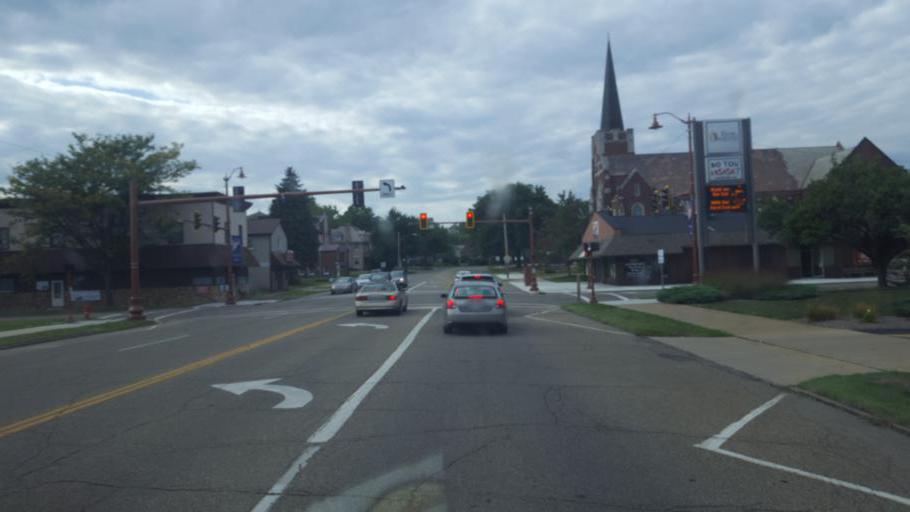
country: US
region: Ohio
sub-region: Tuscarawas County
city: Dover
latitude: 40.5232
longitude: -81.4773
